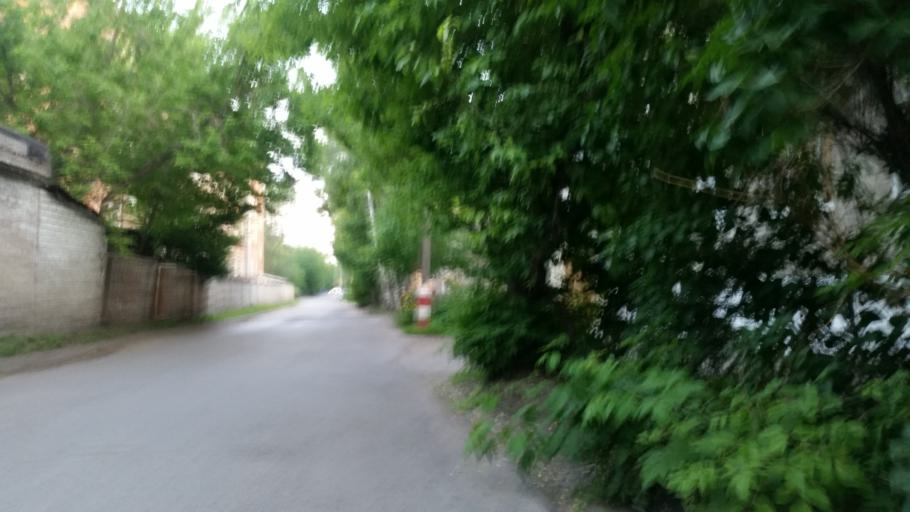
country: RU
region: Ulyanovsk
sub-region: Ulyanovskiy Rayon
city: Ulyanovsk
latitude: 54.3343
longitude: 48.4048
